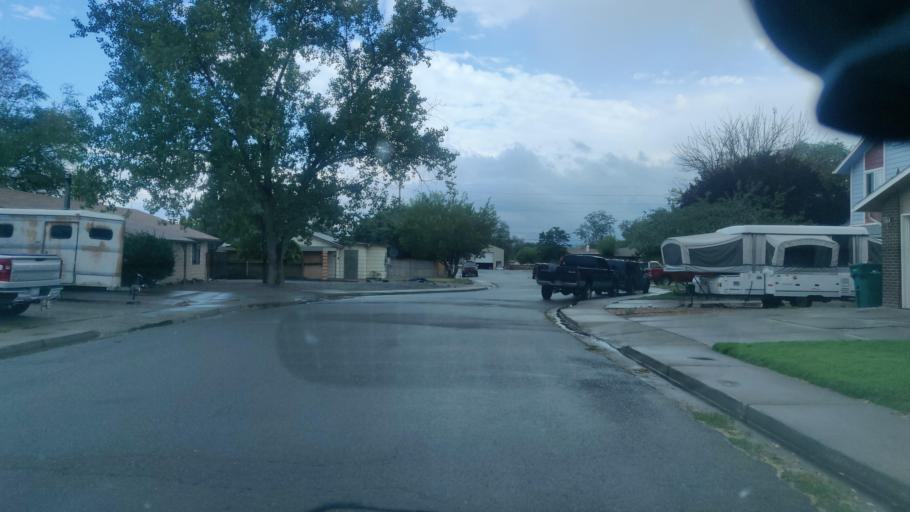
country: US
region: Colorado
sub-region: Mesa County
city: Fruitvale
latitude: 39.0711
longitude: -108.4850
